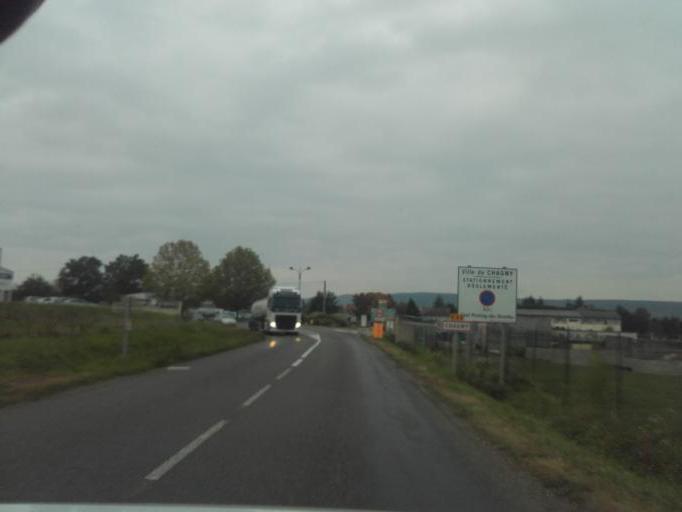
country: FR
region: Bourgogne
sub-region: Departement de Saone-et-Loire
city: Chagny
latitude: 46.9100
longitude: 4.7661
